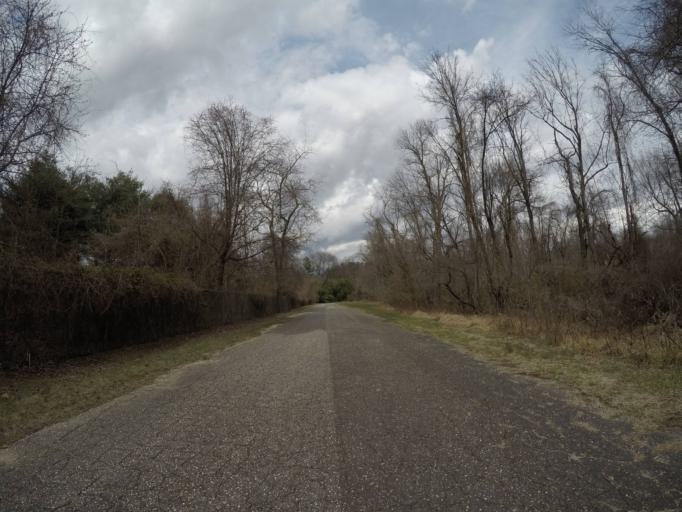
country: US
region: Maryland
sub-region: Howard County
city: Columbia
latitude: 39.2534
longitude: -76.8264
